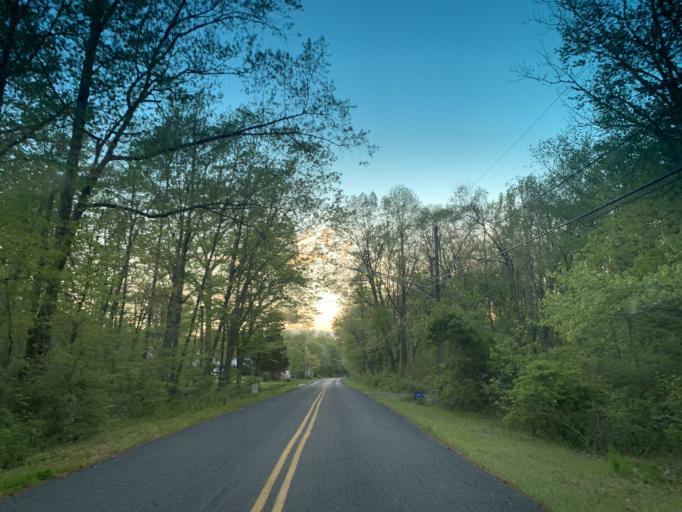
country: US
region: Maryland
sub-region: Harford County
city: Riverside
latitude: 39.5250
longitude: -76.2483
